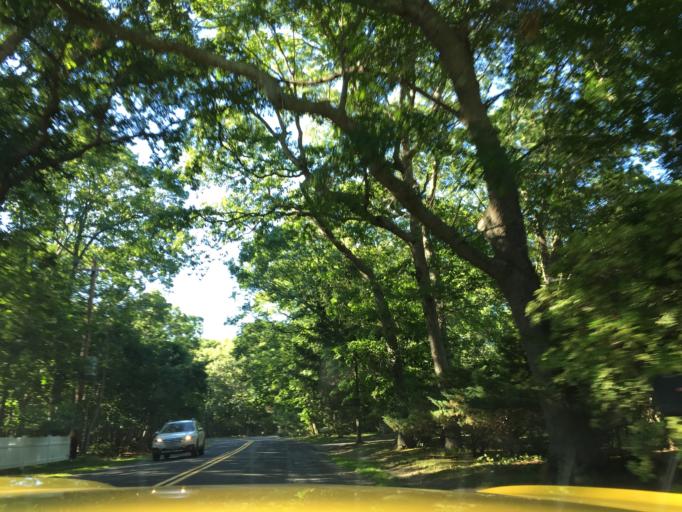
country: US
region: New York
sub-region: Suffolk County
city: Southold
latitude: 41.0441
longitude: -72.4104
